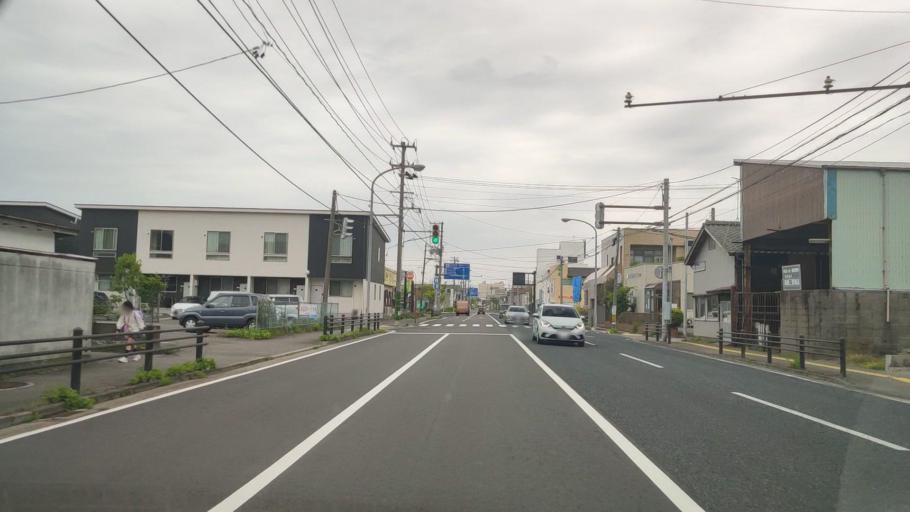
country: JP
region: Niigata
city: Niigata-shi
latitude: 37.9347
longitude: 139.0726
